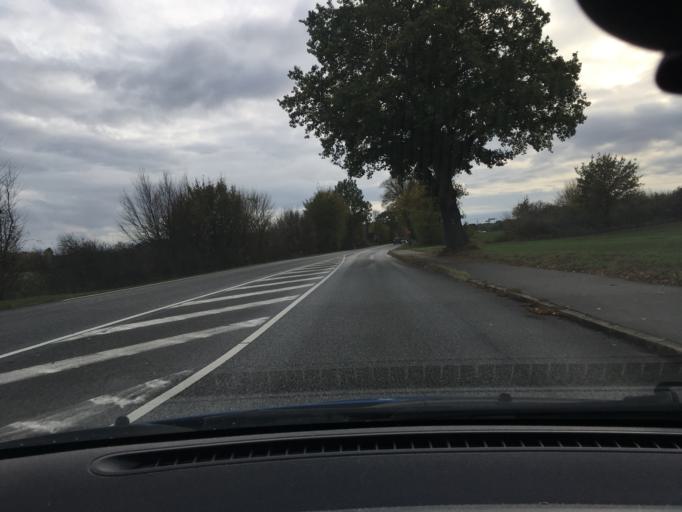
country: DE
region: Schleswig-Holstein
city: Talkau
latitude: 53.5753
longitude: 10.5682
